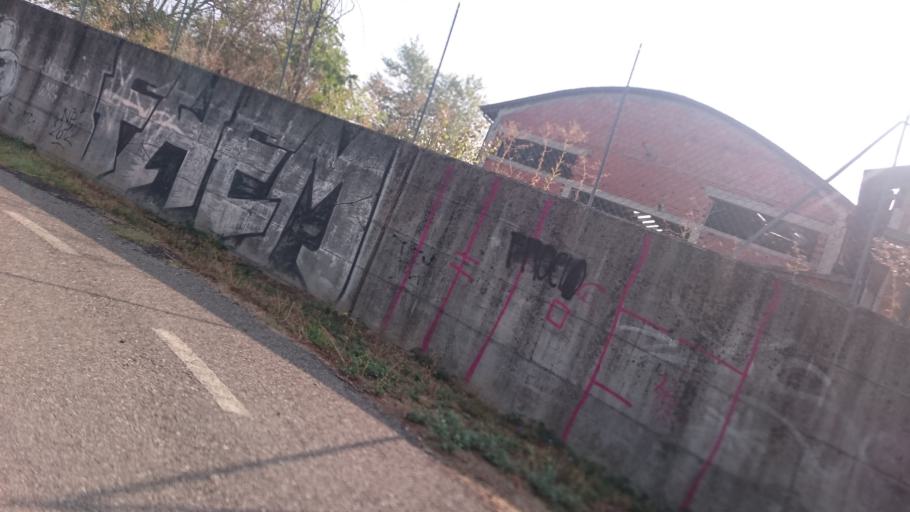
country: IT
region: Emilia-Romagna
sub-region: Provincia di Reggio Emilia
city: Albinea
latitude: 44.6350
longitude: 10.6220
